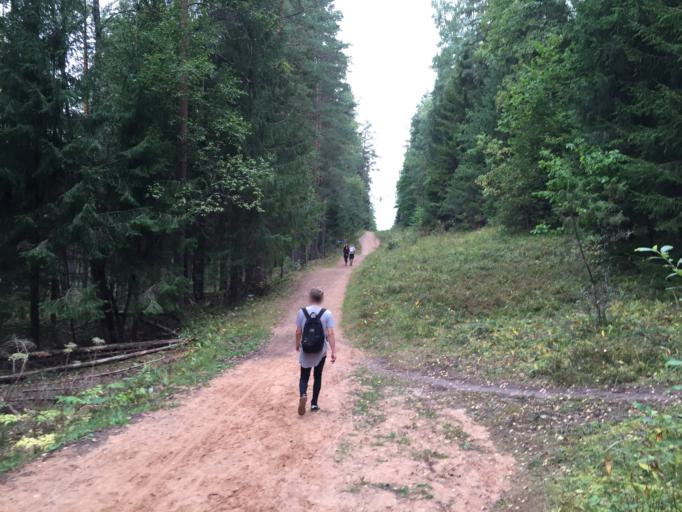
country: LV
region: Ogre
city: Ogre
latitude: 56.8346
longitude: 24.5645
